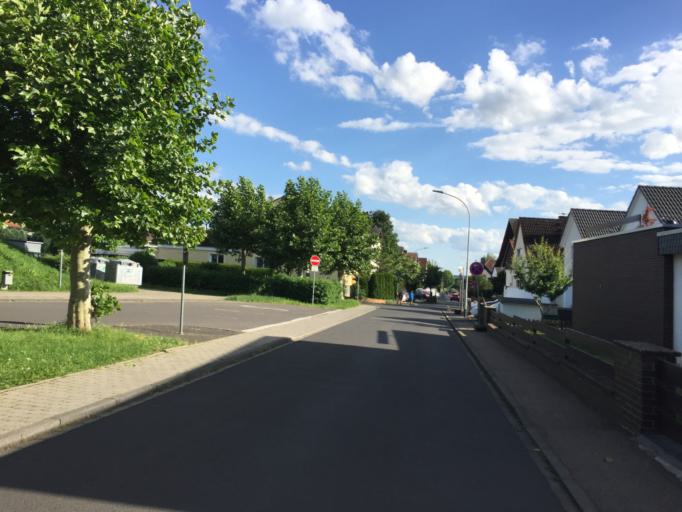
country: DE
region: Hesse
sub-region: Regierungsbezirk Darmstadt
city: Karben
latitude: 50.2346
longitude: 8.7744
